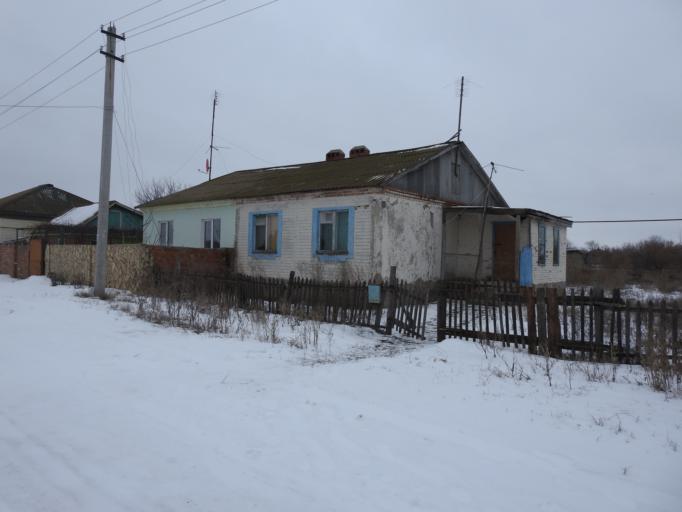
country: RU
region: Saratov
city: Sovetskoye
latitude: 51.5364
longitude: 46.5957
